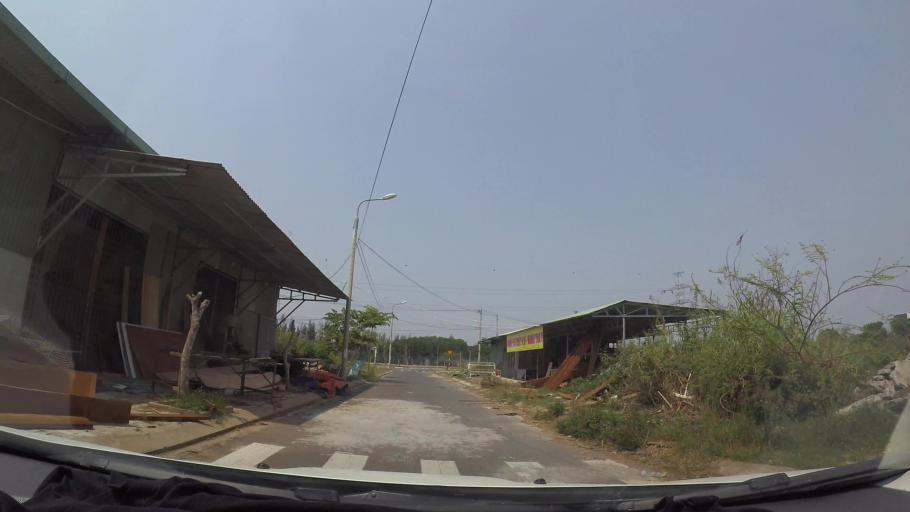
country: VN
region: Da Nang
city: Cam Le
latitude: 15.9931
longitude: 108.2045
